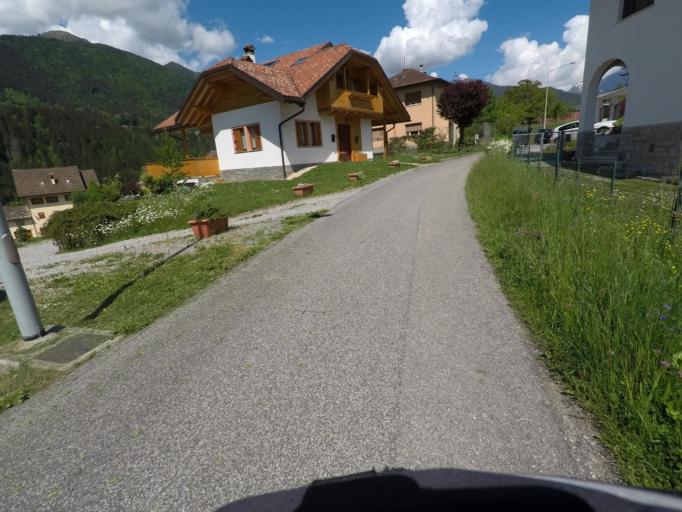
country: IT
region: Friuli Venezia Giulia
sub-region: Provincia di Udine
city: Ovaro
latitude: 46.4804
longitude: 12.8680
